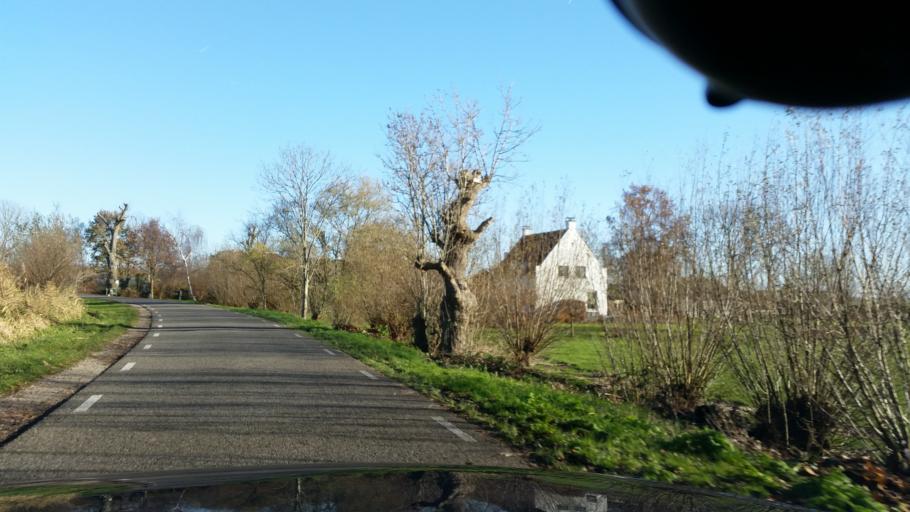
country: NL
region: North Holland
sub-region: Gemeente Ouder-Amstel
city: Ouderkerk aan de Amstel
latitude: 52.2866
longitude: 4.8886
